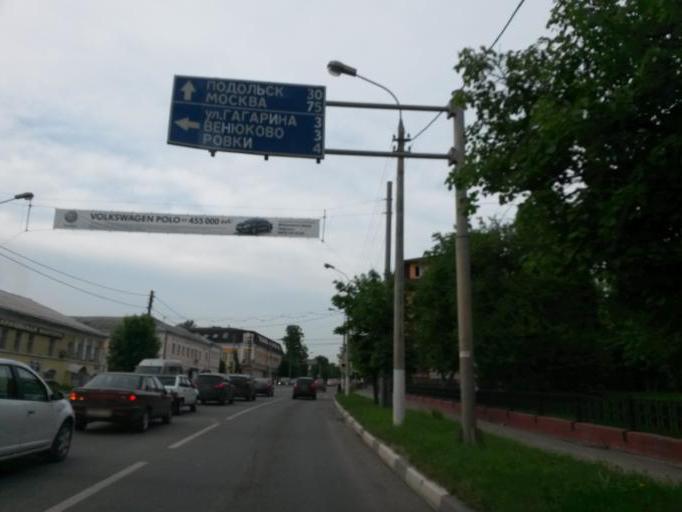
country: RU
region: Moskovskaya
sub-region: Chekhovskiy Rayon
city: Chekhov
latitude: 55.1439
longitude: 37.4531
